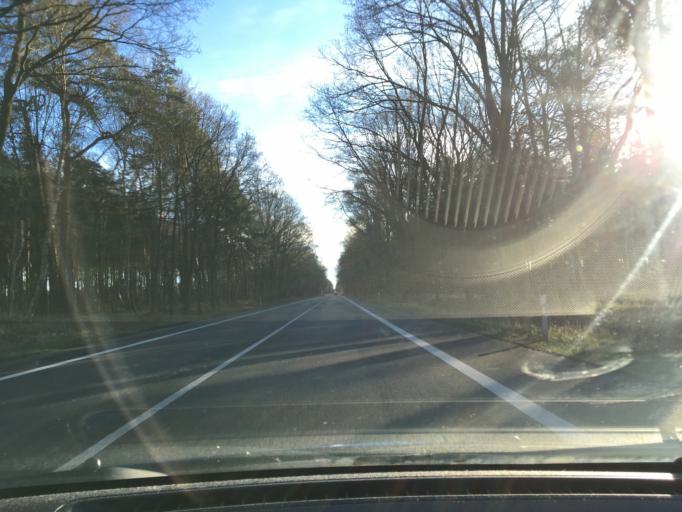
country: DE
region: Lower Saxony
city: Jelmstorf
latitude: 53.1216
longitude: 10.5082
